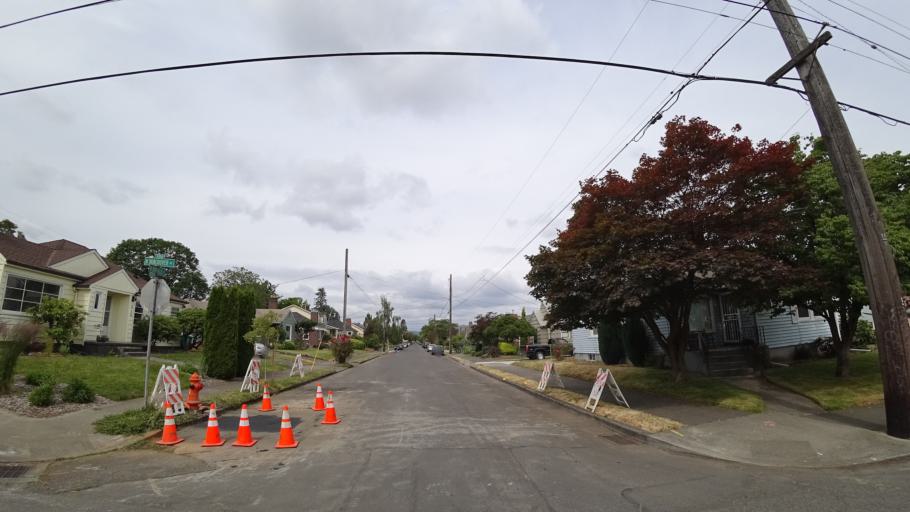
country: US
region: Oregon
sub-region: Multnomah County
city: Portland
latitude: 45.5751
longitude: -122.6687
